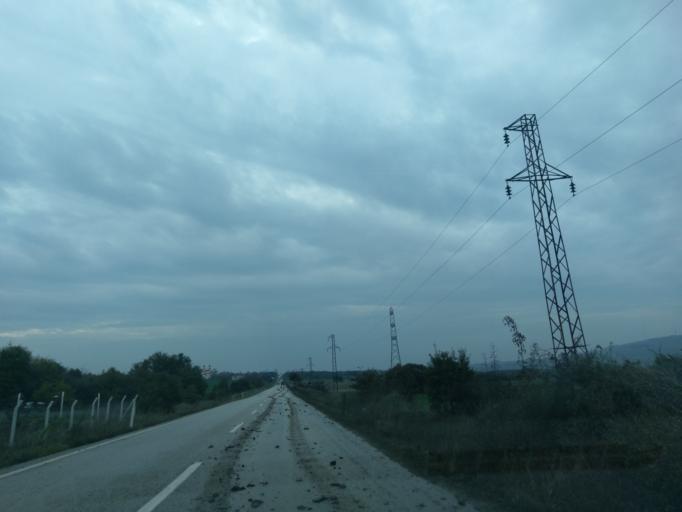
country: TR
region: Istanbul
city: Canta
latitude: 41.1503
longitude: 28.1068
